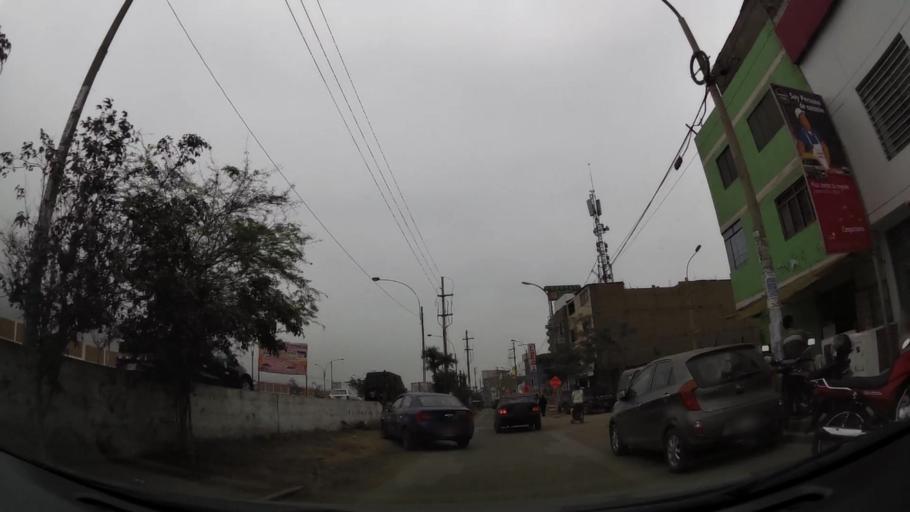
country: PE
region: Lima
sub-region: Lima
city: Urb. Santo Domingo
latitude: -11.9147
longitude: -77.0404
